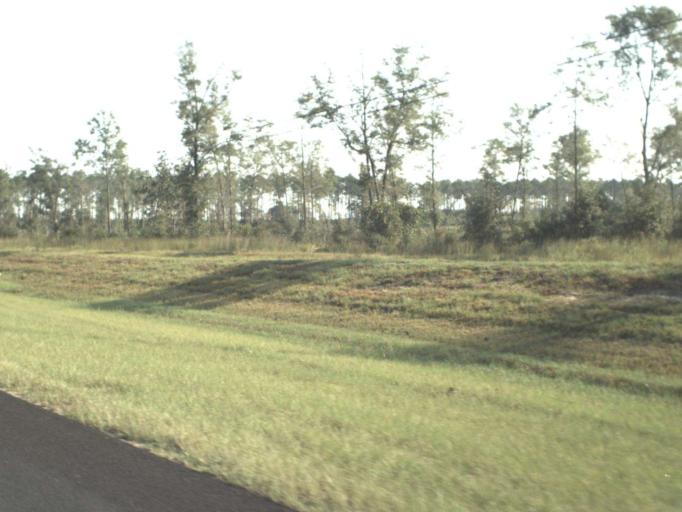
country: US
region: Florida
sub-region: Bay County
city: Laguna Beach
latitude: 30.4817
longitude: -85.8434
